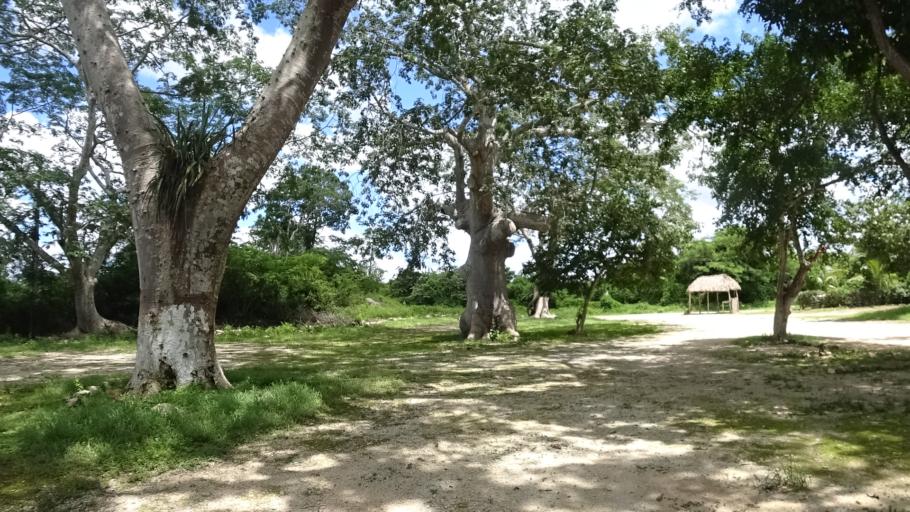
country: MX
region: Yucatan
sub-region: Valladolid
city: Dzitnup
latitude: 20.6689
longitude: -88.2294
